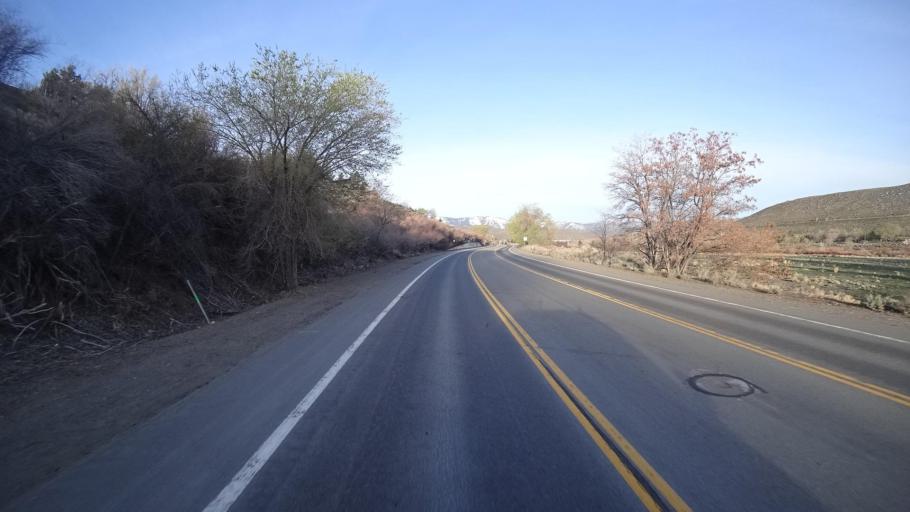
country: US
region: Nevada
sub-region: Washoe County
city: Mogul
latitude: 39.5059
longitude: -119.8773
